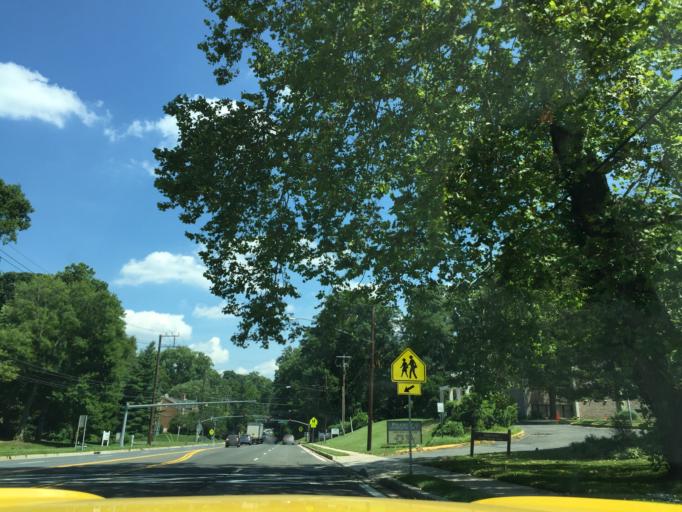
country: US
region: Maryland
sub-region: Montgomery County
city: Somerset
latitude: 38.9589
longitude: -77.1113
